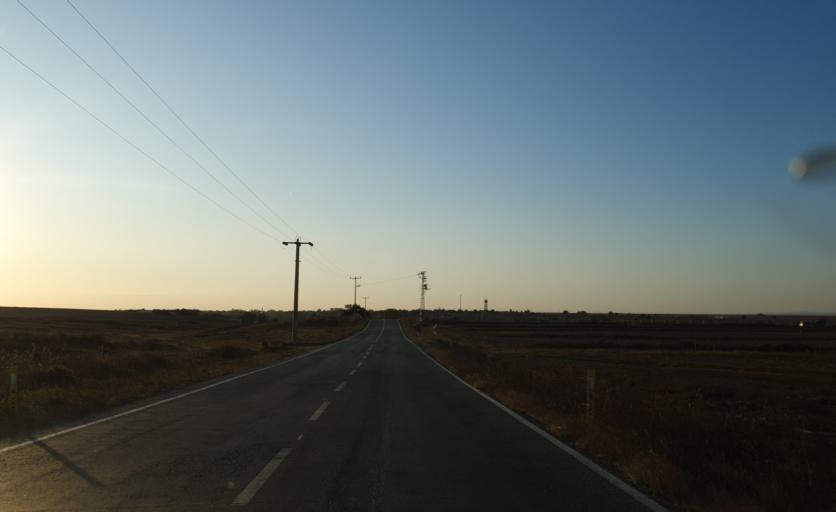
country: TR
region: Tekirdag
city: Beyazkoy
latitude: 41.3415
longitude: 27.7253
